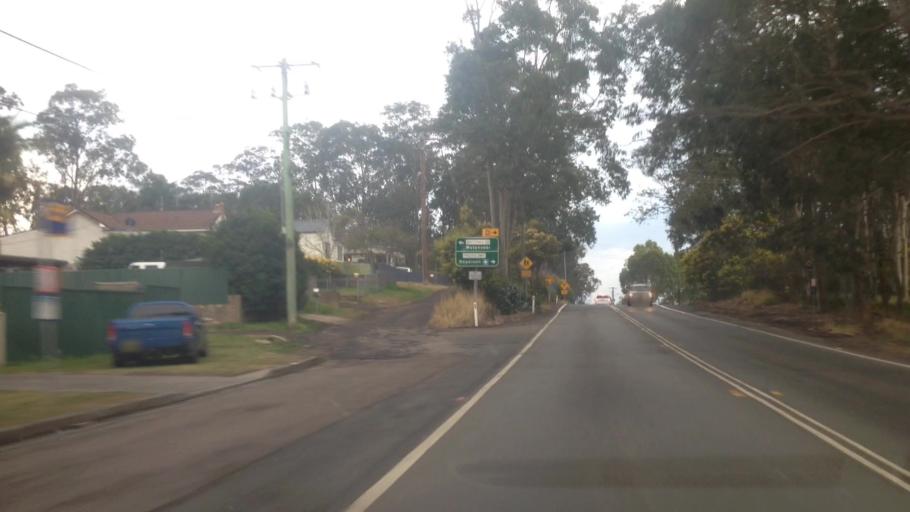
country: AU
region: New South Wales
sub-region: Wyong Shire
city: Jilliby
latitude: -33.2695
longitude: 151.4315
